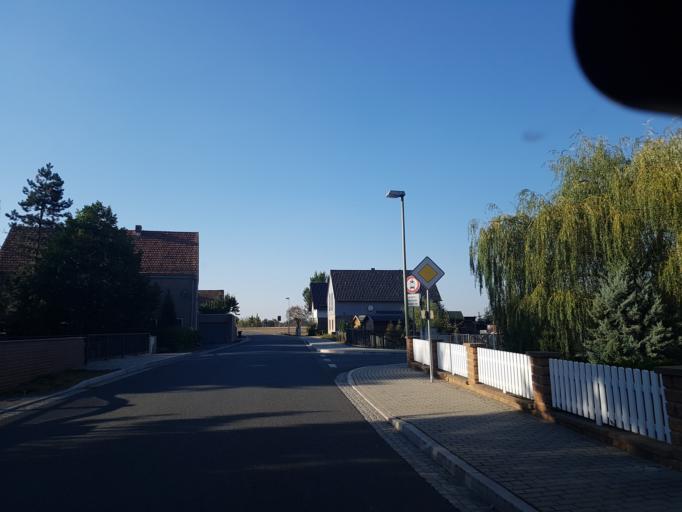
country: DE
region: Saxony
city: Nauwalde
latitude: 51.4479
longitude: 13.3911
